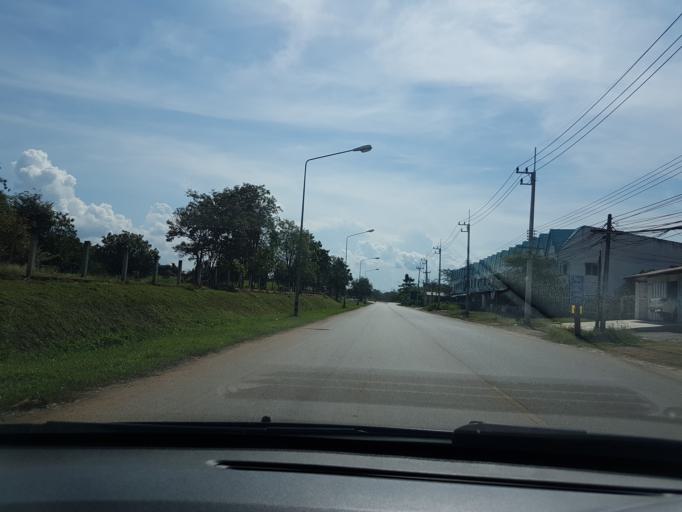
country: TH
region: Lampang
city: Ko Kha
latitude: 18.2109
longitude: 99.3898
